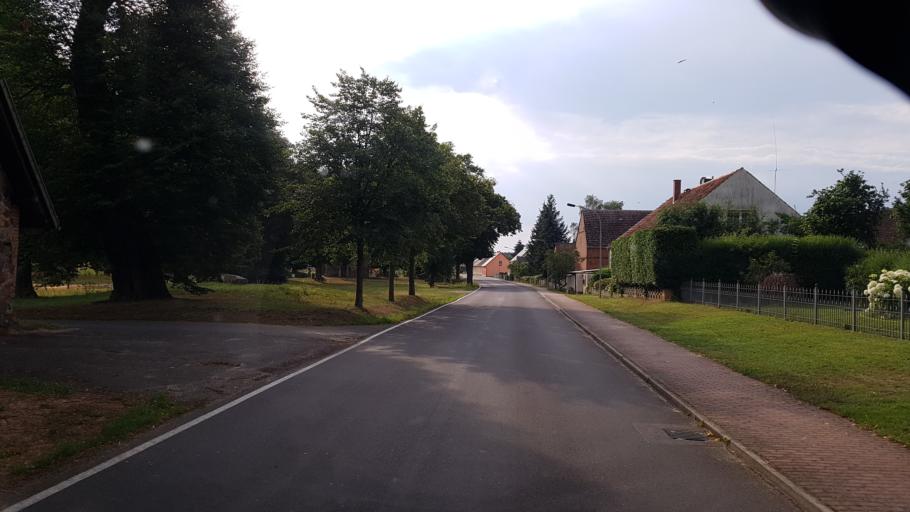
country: DE
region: Brandenburg
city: Dahme
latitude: 51.9509
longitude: 13.4704
